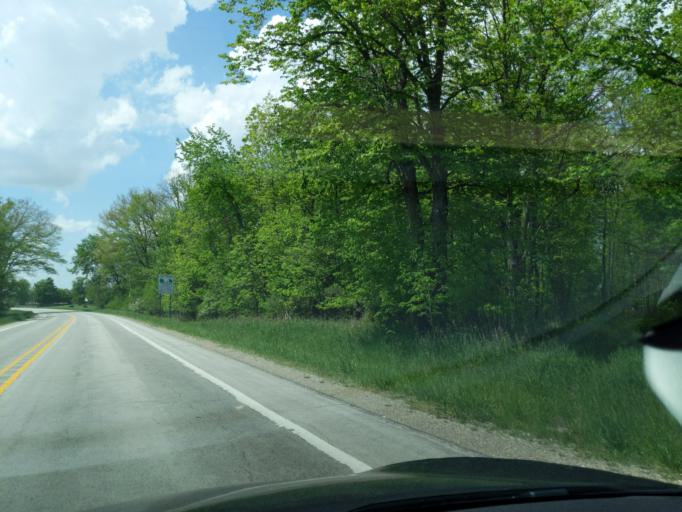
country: US
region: Michigan
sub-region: Ingham County
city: Stockbridge
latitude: 42.5542
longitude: -84.2345
